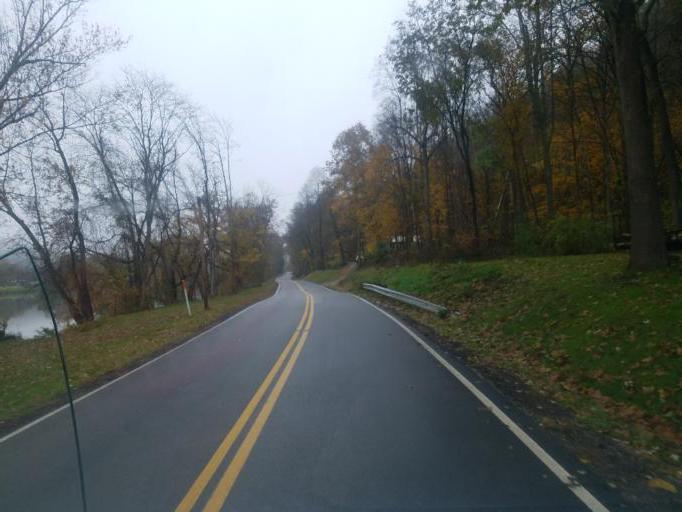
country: US
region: Ohio
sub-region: Morgan County
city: McConnelsville
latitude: 39.5908
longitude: -81.8038
